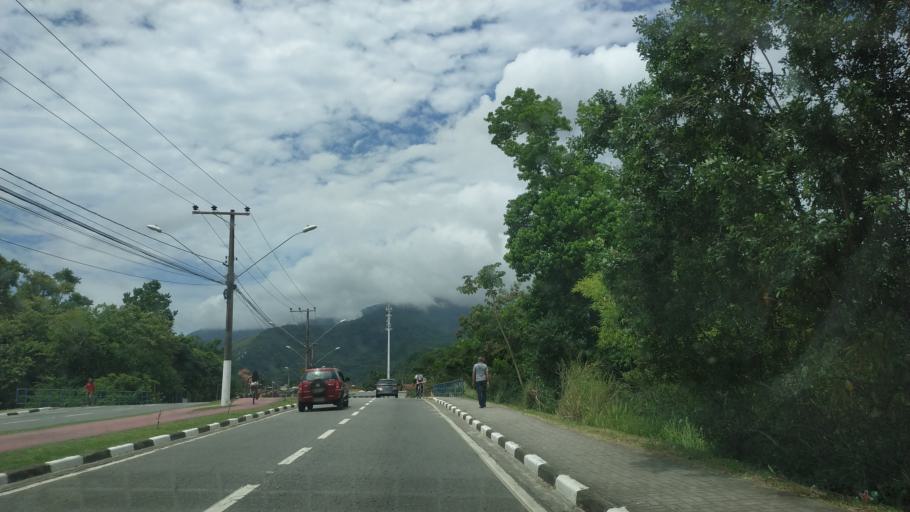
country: BR
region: Sao Paulo
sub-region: Ilhabela
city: Ilhabela
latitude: -23.8200
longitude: -45.3688
